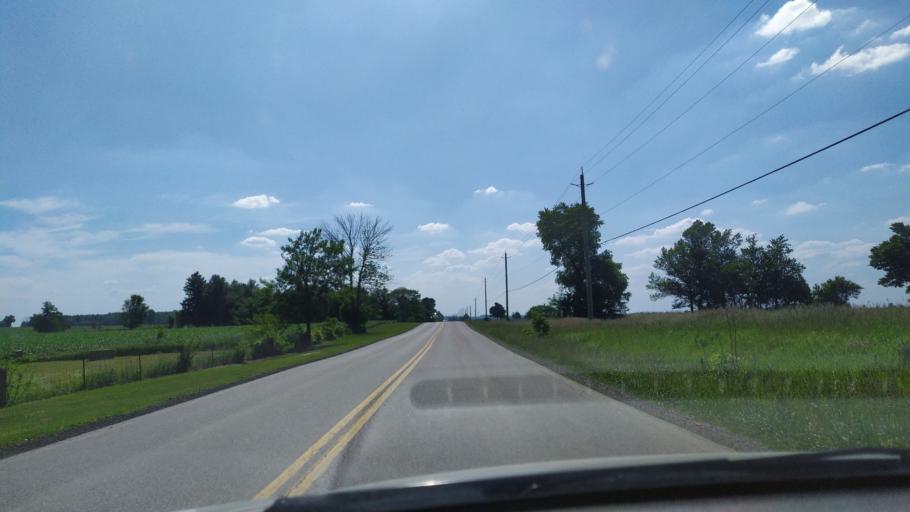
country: CA
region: Ontario
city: Kitchener
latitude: 43.3662
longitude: -80.5925
